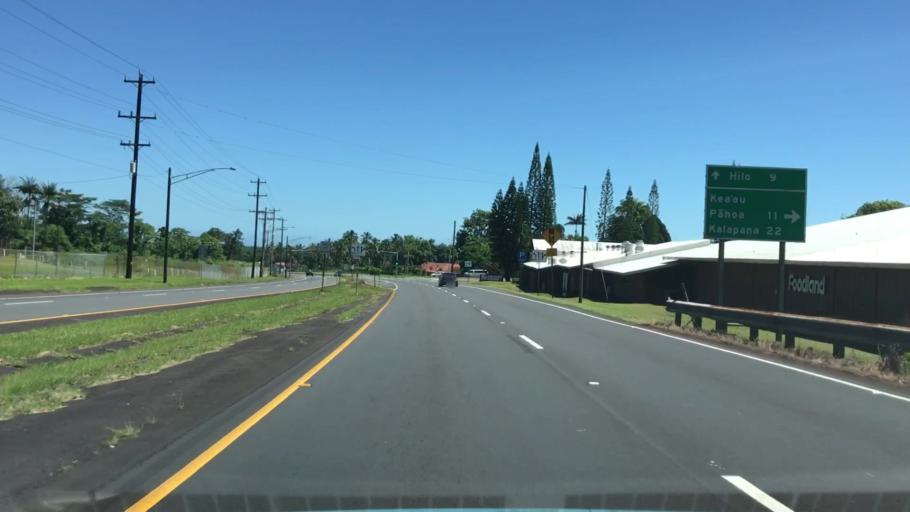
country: US
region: Hawaii
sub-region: Hawaii County
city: Kea'au
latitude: 19.6217
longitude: -155.0415
